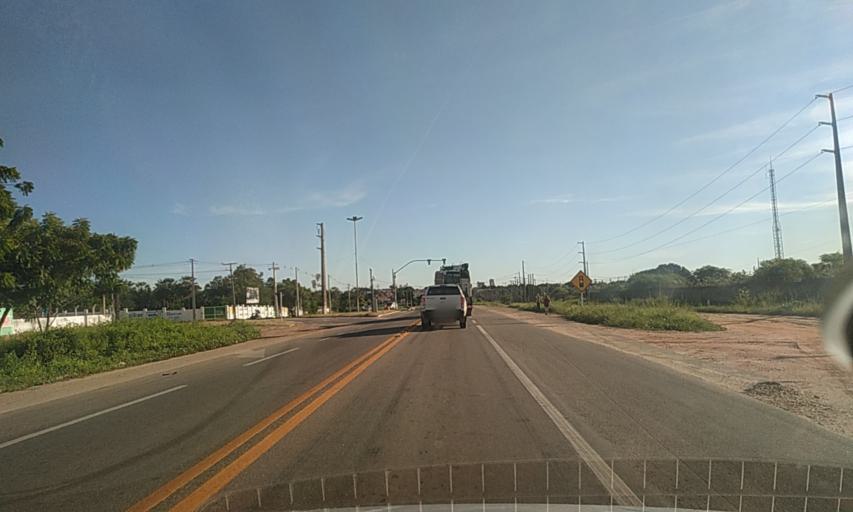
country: BR
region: Rio Grande do Norte
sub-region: Mossoro
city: Mossoro
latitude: -5.1931
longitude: -37.3119
